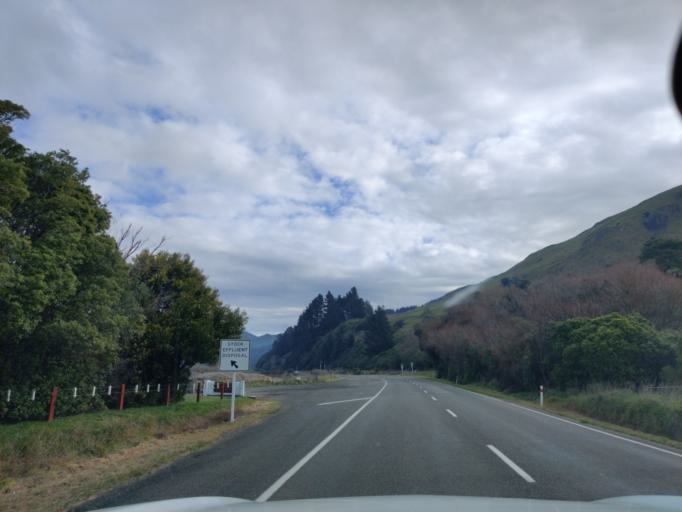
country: NZ
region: Manawatu-Wanganui
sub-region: Palmerston North City
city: Palmerston North
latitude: -40.3362
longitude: 175.8350
